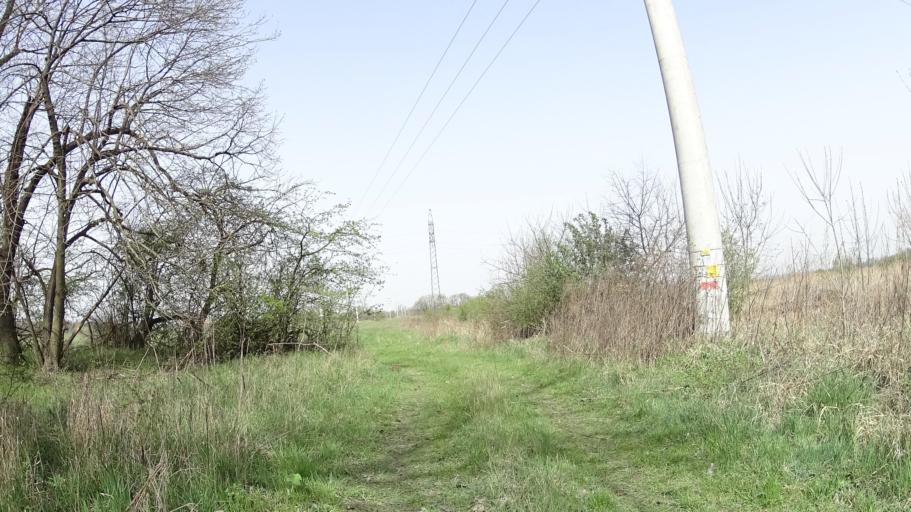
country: HU
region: Budapest
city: Budapest XXIII. keruelet
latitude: 47.3682
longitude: 19.1534
